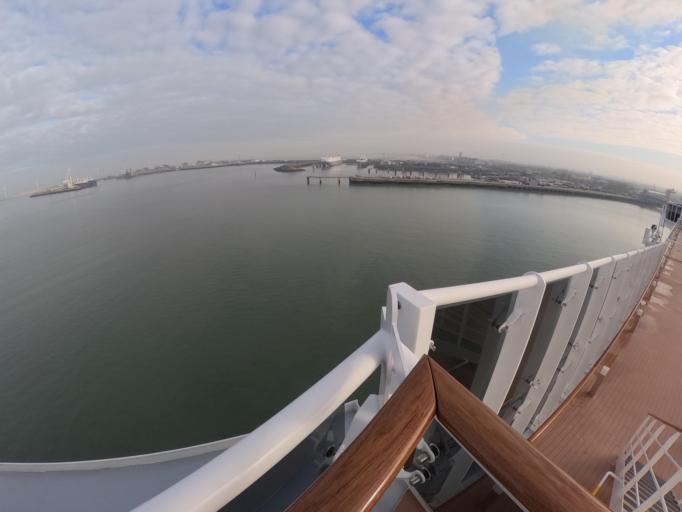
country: BE
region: Flanders
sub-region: Provincie West-Vlaanderen
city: Zeebrugge
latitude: 51.3405
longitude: 3.2065
